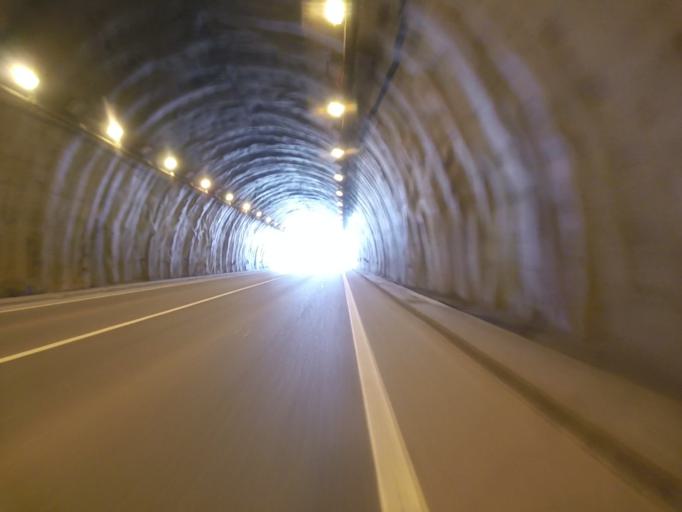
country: ES
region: Basque Country
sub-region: Provincia de Guipuzcoa
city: Azkoitia
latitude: 43.1721
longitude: -2.3080
